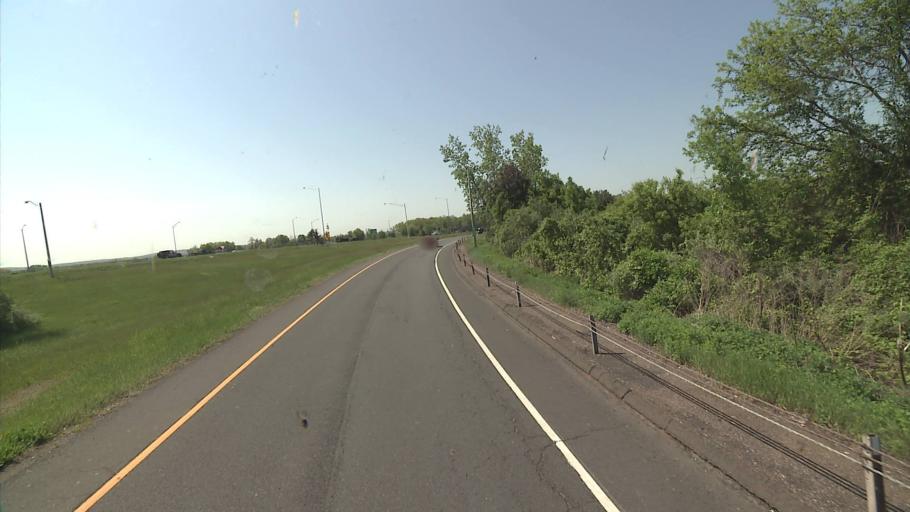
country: US
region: Connecticut
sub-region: Hartford County
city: Manchester
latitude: 41.8007
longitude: -72.5568
